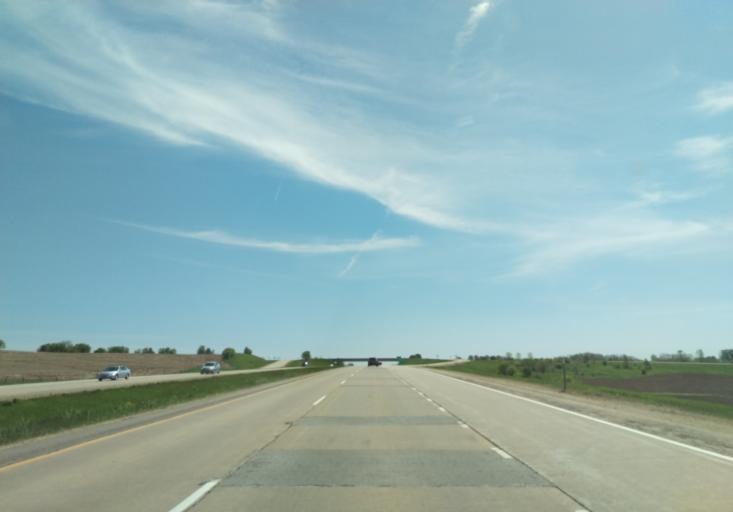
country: US
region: Wisconsin
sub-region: Dane County
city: Verona
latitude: 42.9875
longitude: -89.5889
